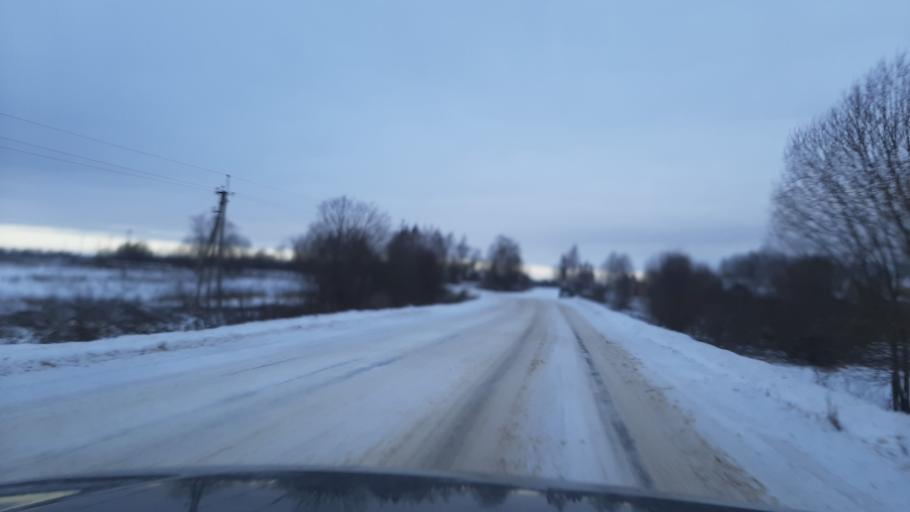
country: RU
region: Kostroma
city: Volgorechensk
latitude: 57.4476
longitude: 41.0307
